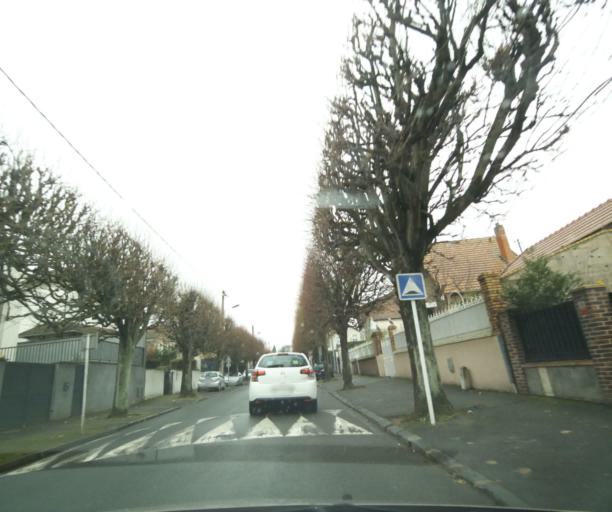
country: FR
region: Ile-de-France
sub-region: Departement du Val-de-Marne
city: Ablon-sur-Seine
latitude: 48.7371
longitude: 2.4161
